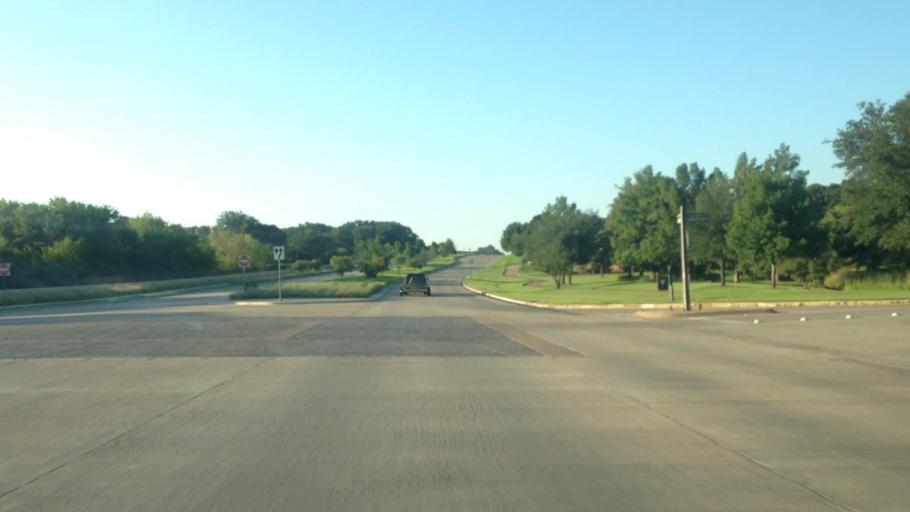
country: US
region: Texas
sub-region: Denton County
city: Trophy Club
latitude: 32.9711
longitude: -97.1862
